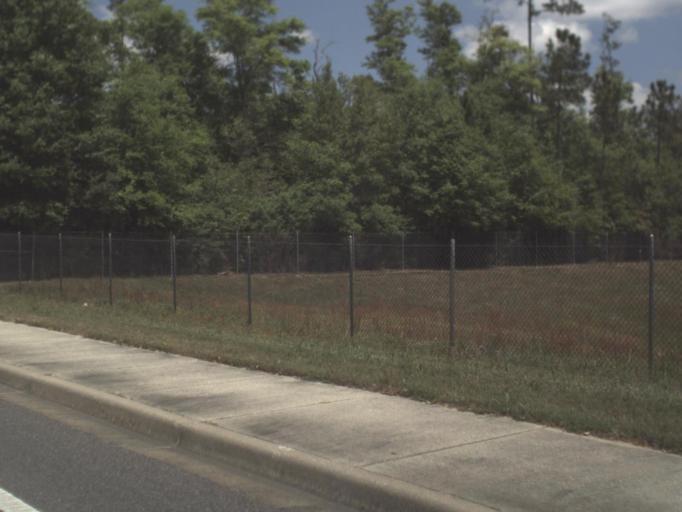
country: US
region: Florida
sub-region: Santa Rosa County
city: Point Baker
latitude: 30.6698
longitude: -87.0543
